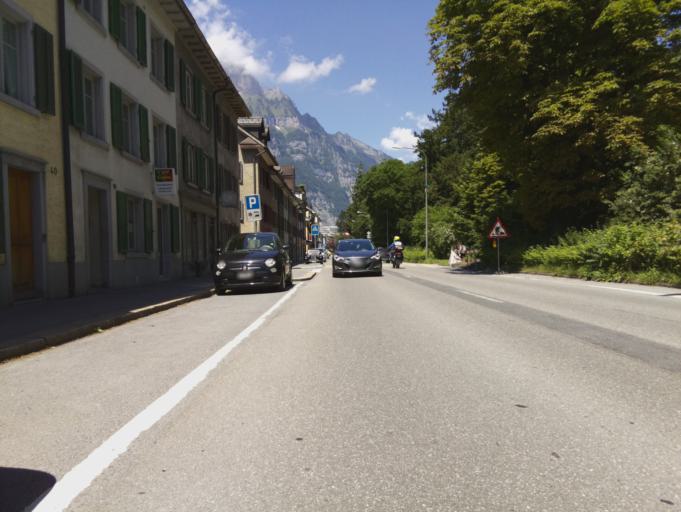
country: CH
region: Glarus
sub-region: Glarus
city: Glarus
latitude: 47.0380
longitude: 9.0711
